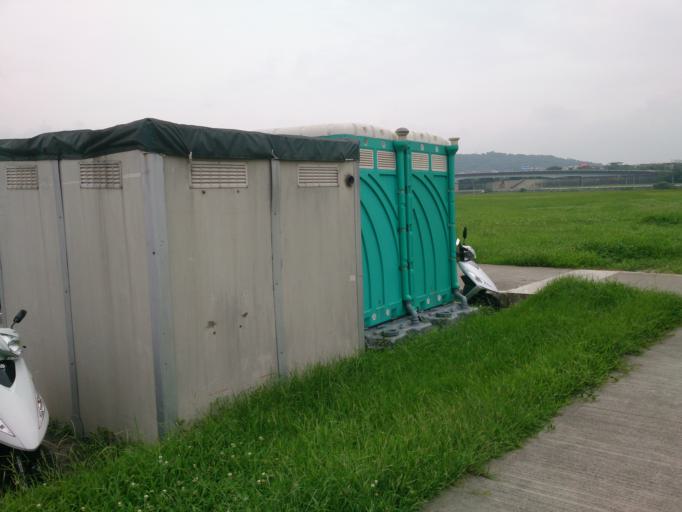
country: TW
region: Taipei
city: Taipei
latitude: 25.0683
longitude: 121.5688
